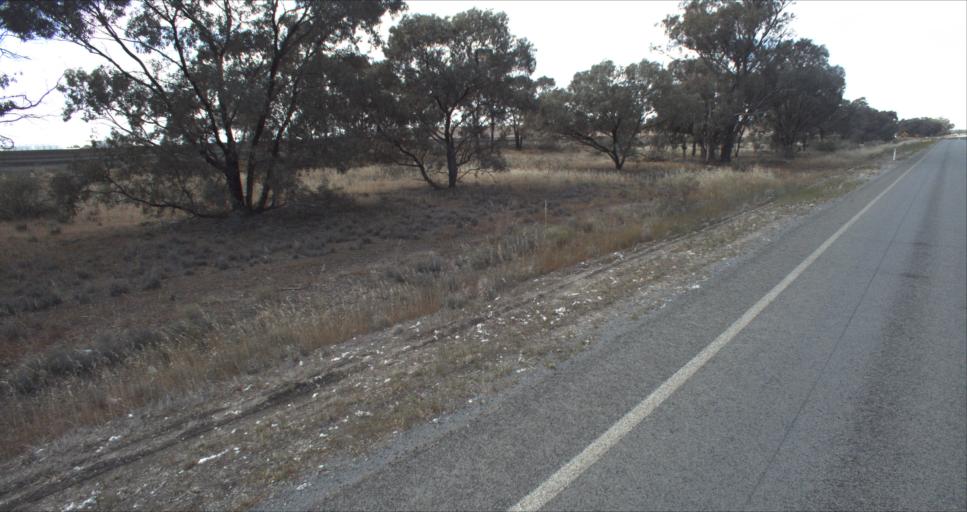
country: AU
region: New South Wales
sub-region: Murrumbidgee Shire
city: Darlington Point
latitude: -34.5717
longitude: 146.1670
